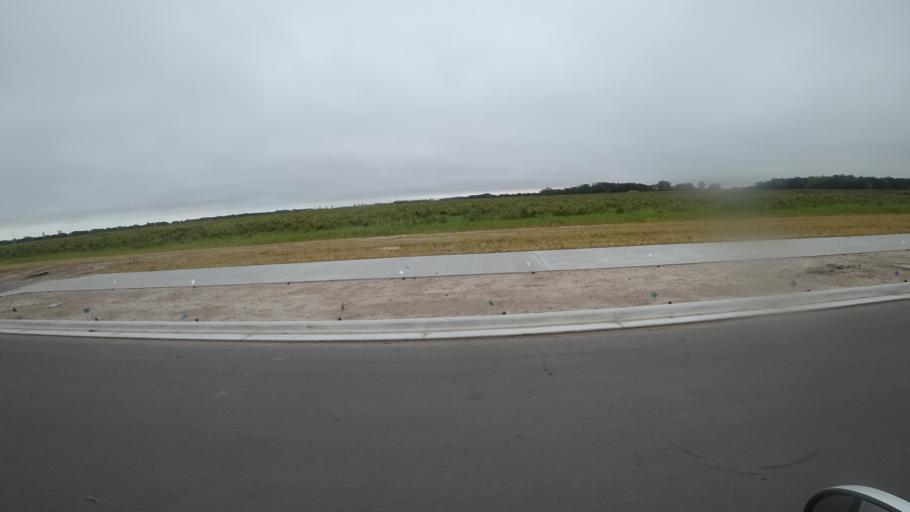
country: US
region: Florida
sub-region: Sarasota County
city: The Meadows
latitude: 27.4527
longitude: -82.3510
